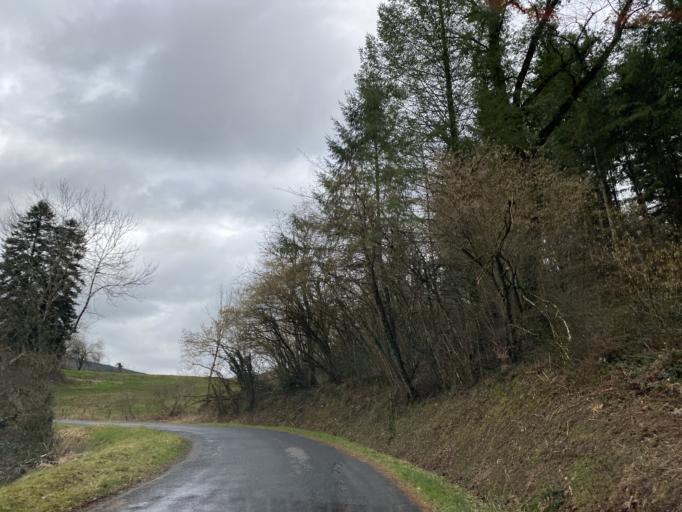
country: FR
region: Auvergne
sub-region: Departement du Puy-de-Dome
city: Escoutoux
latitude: 45.8150
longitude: 3.6045
